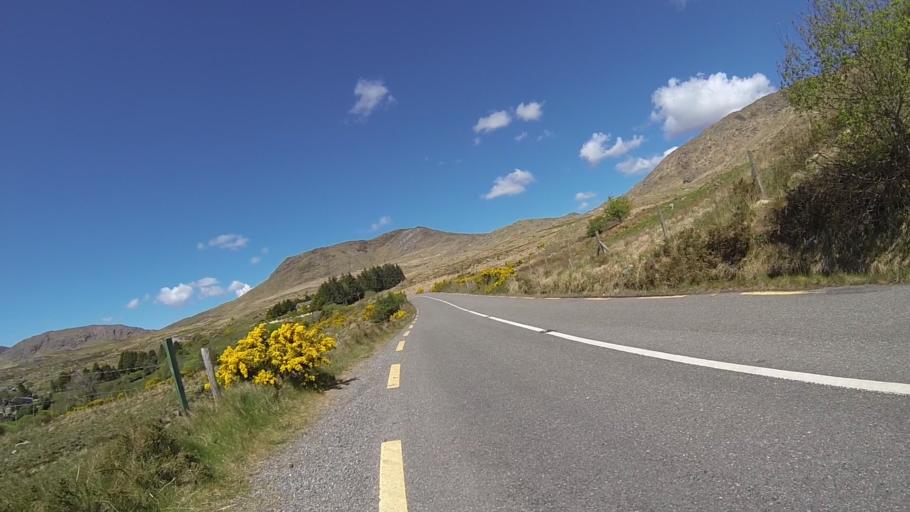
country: IE
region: Munster
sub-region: Ciarrai
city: Kenmare
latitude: 51.9235
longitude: -9.6313
